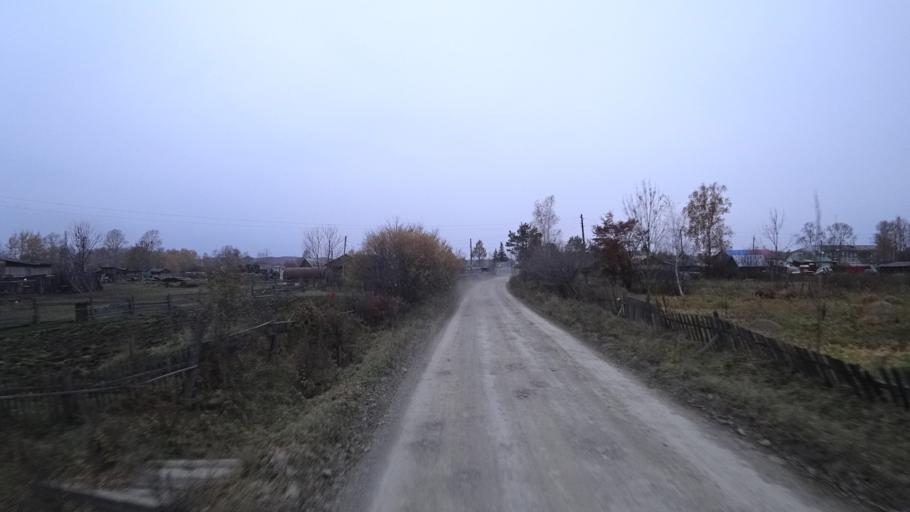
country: RU
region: Khabarovsk Krai
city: Amursk
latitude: 49.8988
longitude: 136.1418
